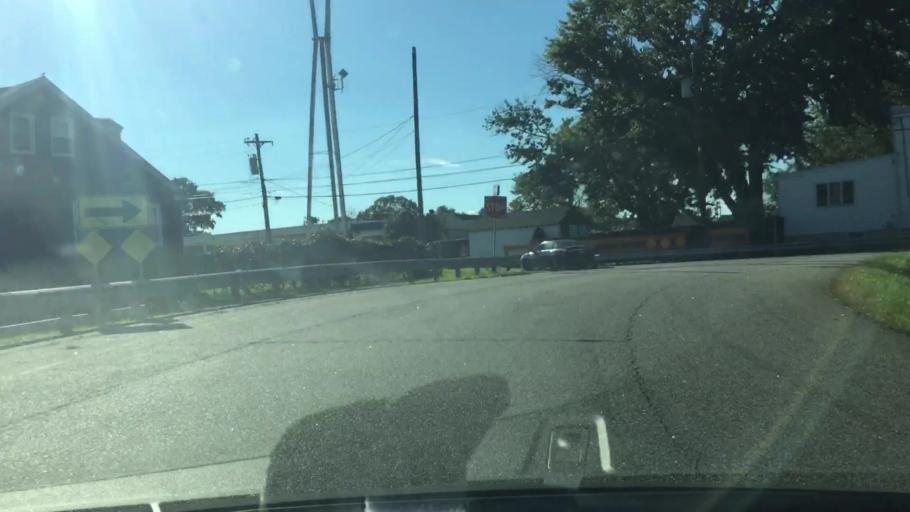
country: US
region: Pennsylvania
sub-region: Delaware County
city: Linwood
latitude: 39.8295
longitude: -75.4322
